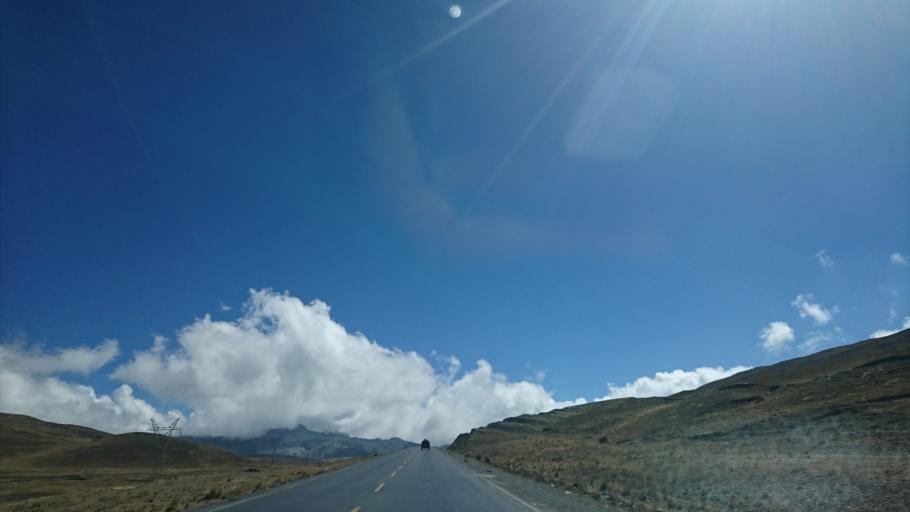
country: BO
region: La Paz
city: La Paz
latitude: -16.3576
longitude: -68.0420
